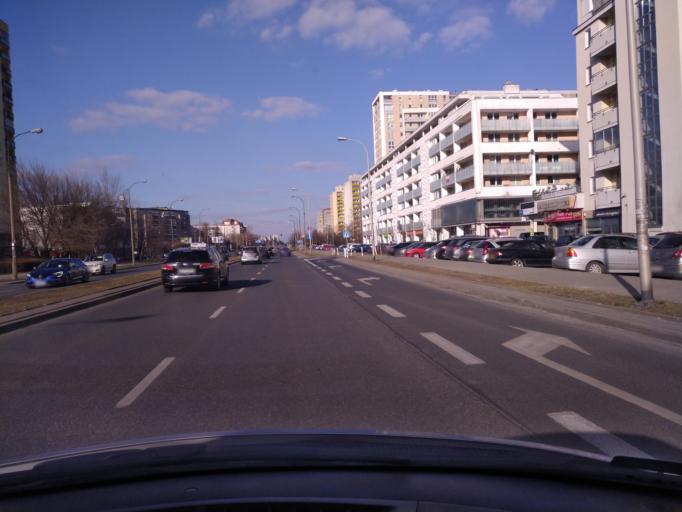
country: PL
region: Masovian Voivodeship
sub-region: Warszawa
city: Praga Poludnie
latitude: 52.2229
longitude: 21.0916
